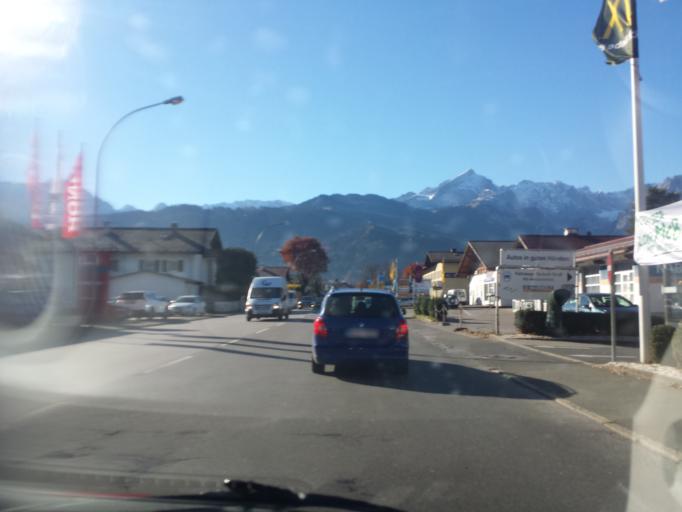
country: DE
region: Bavaria
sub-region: Upper Bavaria
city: Garmisch-Partenkirchen
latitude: 47.5023
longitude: 11.1024
